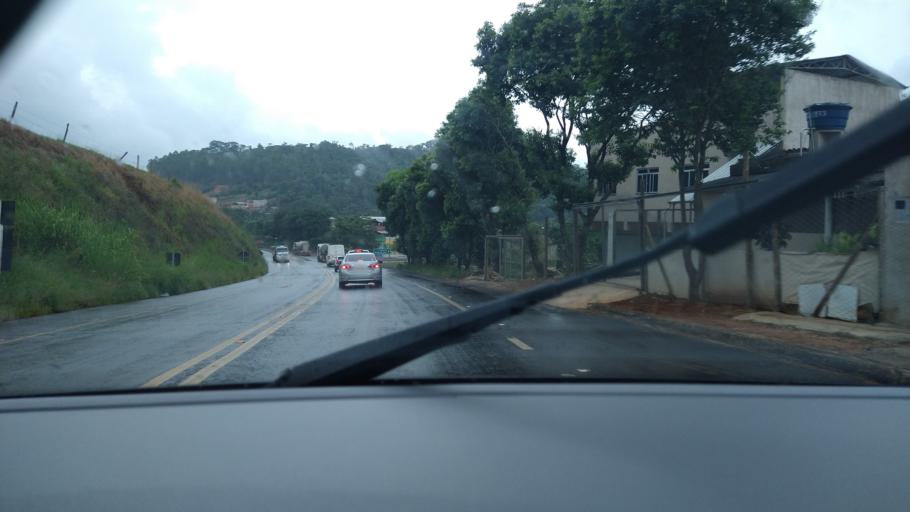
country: BR
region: Minas Gerais
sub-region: Vicosa
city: Vicosa
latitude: -20.6427
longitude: -42.8654
